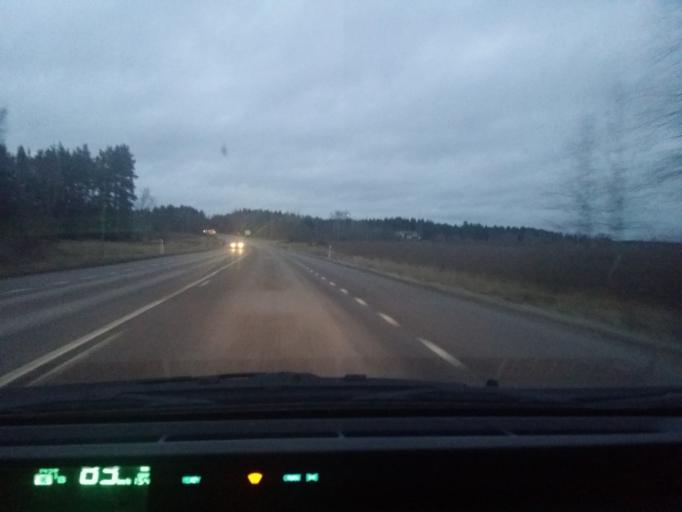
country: SE
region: Vaestmanland
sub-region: Hallstahammars Kommun
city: Kolback
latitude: 59.5720
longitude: 16.3516
